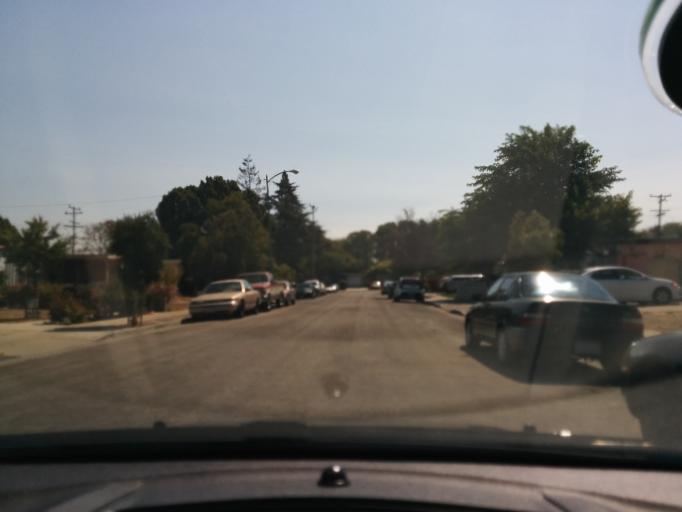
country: US
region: California
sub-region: Santa Clara County
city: Sunnyvale
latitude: 37.3903
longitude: -121.9995
